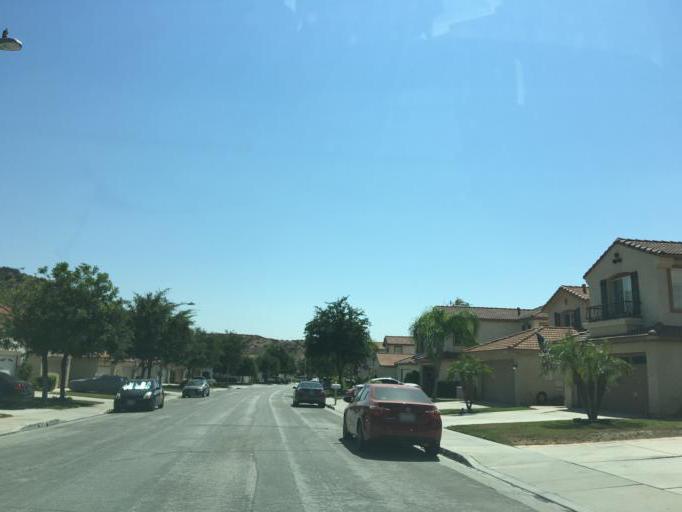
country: US
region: California
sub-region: Los Angeles County
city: Santa Clarita
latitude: 34.3925
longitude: -118.5865
